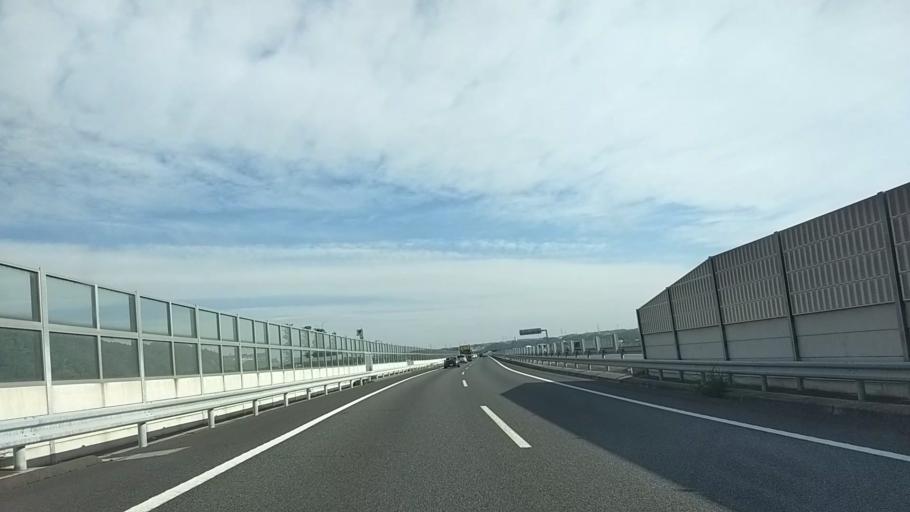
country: JP
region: Kanagawa
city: Zama
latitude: 35.5014
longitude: 139.3657
